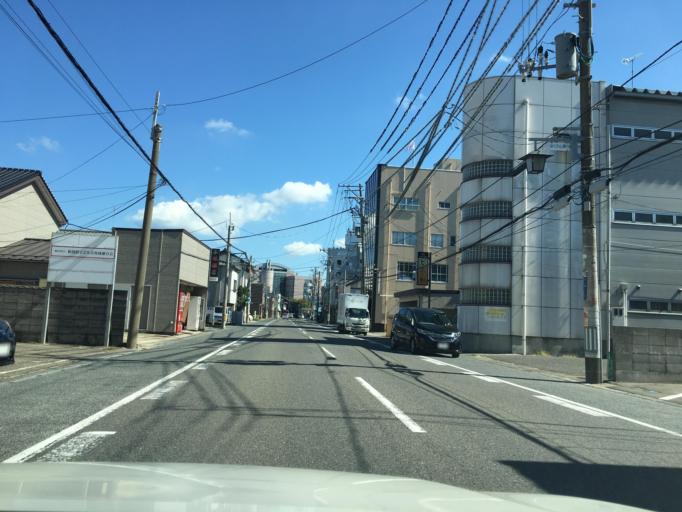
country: JP
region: Niigata
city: Niigata-shi
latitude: 37.9142
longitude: 139.0325
